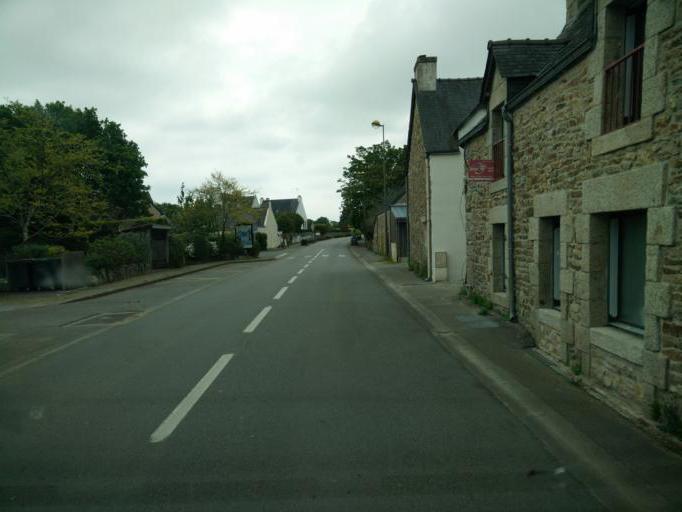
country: FR
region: Brittany
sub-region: Departement du Finistere
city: Tregunc
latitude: 47.8493
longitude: -3.8495
